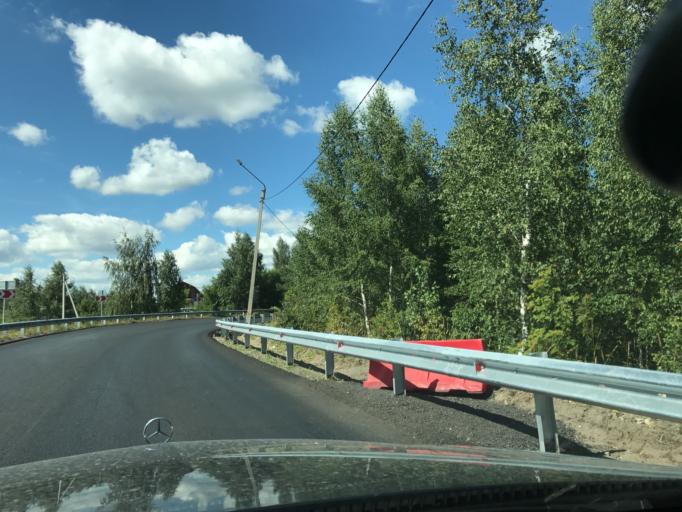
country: RU
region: Nizjnij Novgorod
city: Gorbatovka
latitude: 56.2207
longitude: 43.7463
